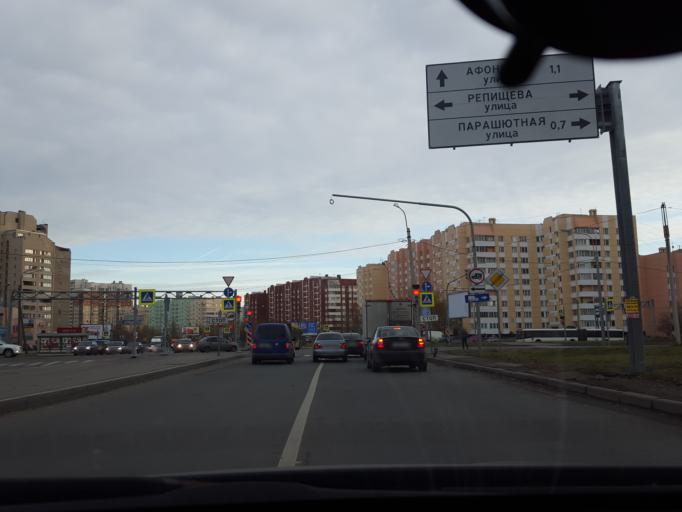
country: RU
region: St.-Petersburg
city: Kolomyagi
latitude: 60.0234
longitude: 30.2803
